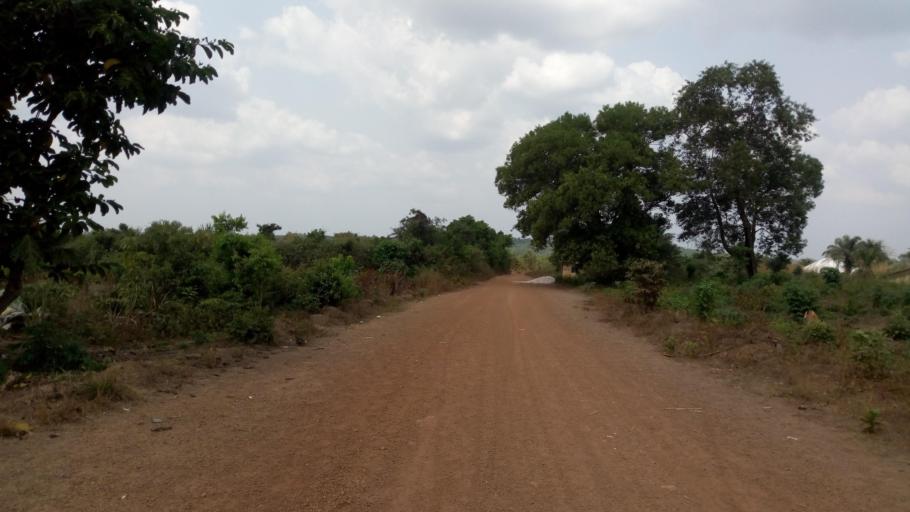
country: SL
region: Southern Province
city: Mogbwemo
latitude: 7.7921
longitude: -12.3071
